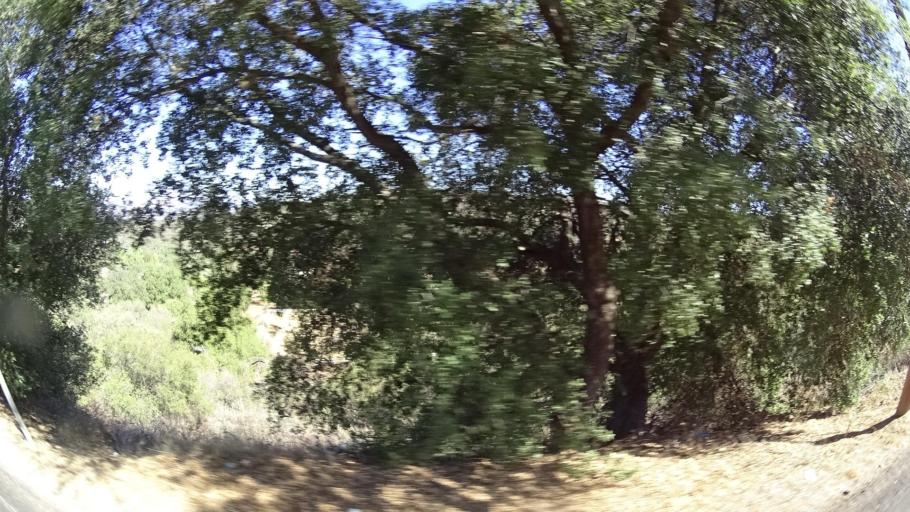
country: US
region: California
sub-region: San Diego County
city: Jamul
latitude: 32.7291
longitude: -116.7832
